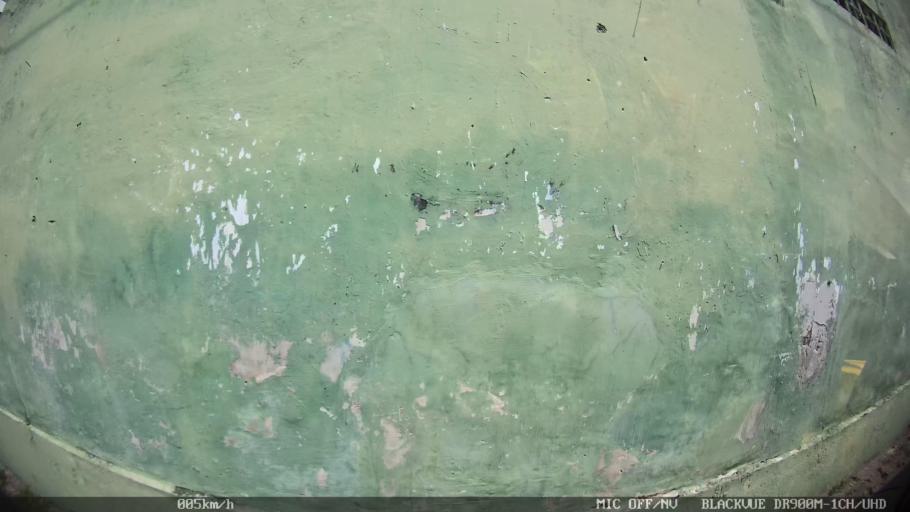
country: ID
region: Daerah Istimewa Yogyakarta
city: Yogyakarta
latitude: -7.8033
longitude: 110.3858
